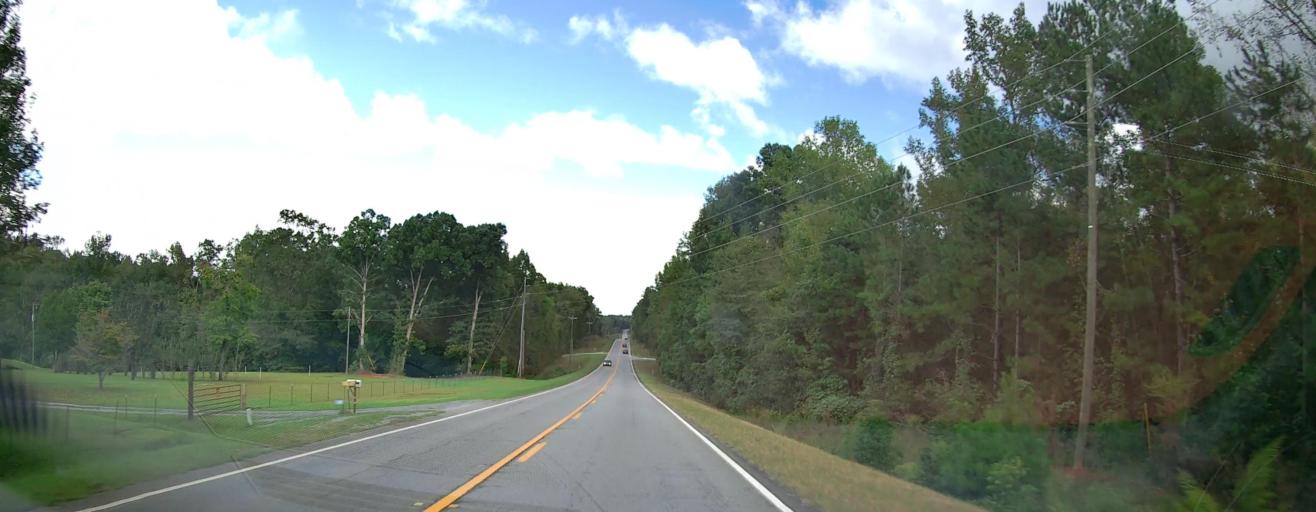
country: US
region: Georgia
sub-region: Jones County
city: Gray
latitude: 32.9681
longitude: -83.4274
